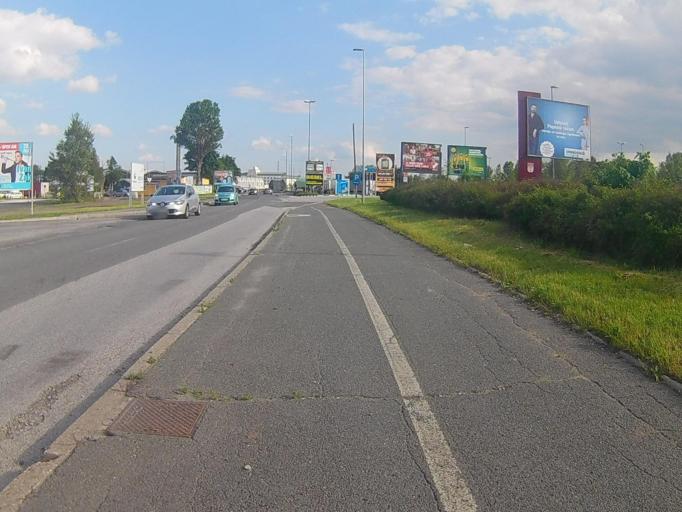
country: SI
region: Maribor
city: Razvanje
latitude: 46.5300
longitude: 15.6463
